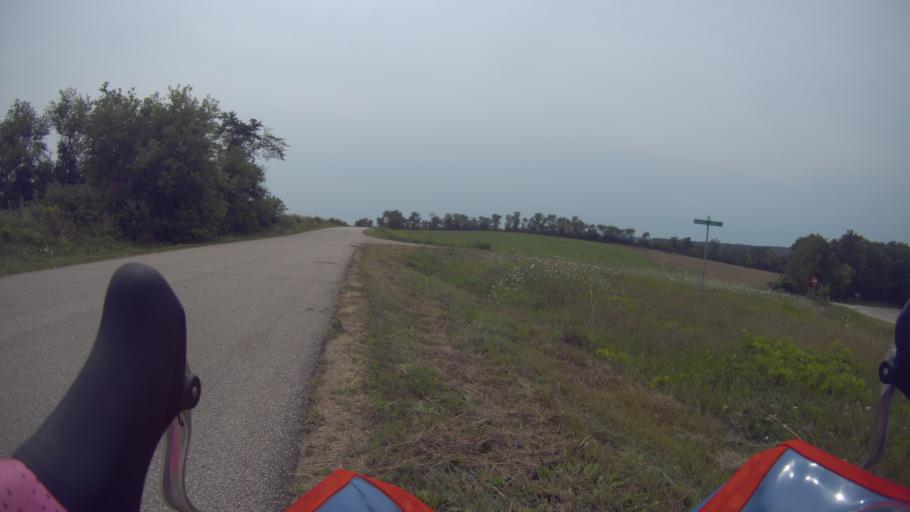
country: US
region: Wisconsin
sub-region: Dane County
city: Mount Horeb
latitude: 42.9383
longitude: -89.6637
